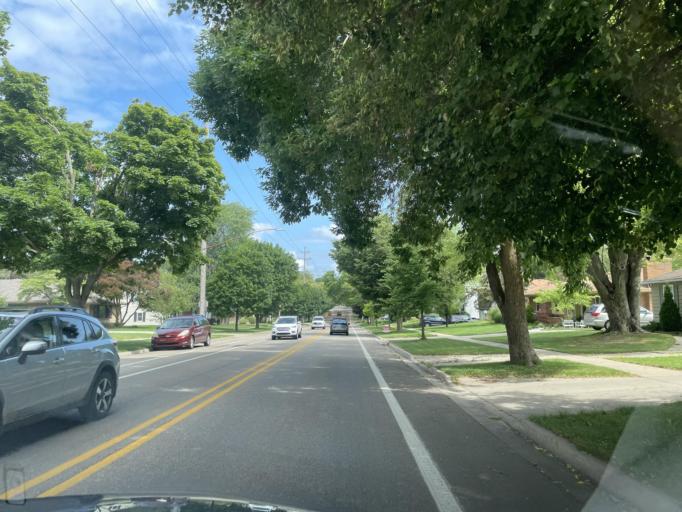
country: US
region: Michigan
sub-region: Kent County
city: East Grand Rapids
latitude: 42.9313
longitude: -85.6242
